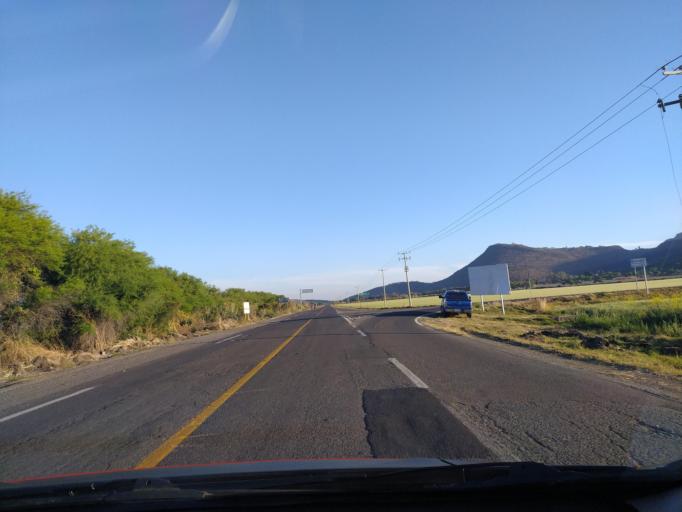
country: MX
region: Guanajuato
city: Ciudad Manuel Doblado
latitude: 20.7795
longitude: -101.8331
